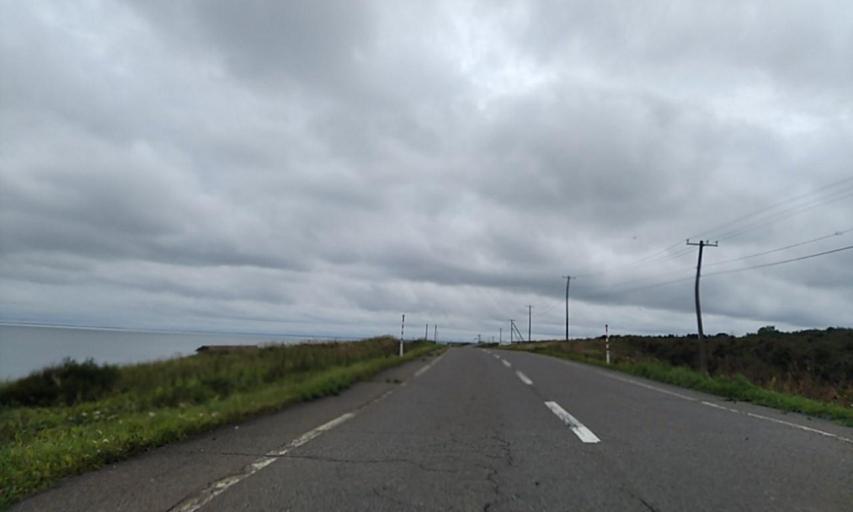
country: JP
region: Hokkaido
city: Shibetsu
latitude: 43.4341
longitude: 145.2631
